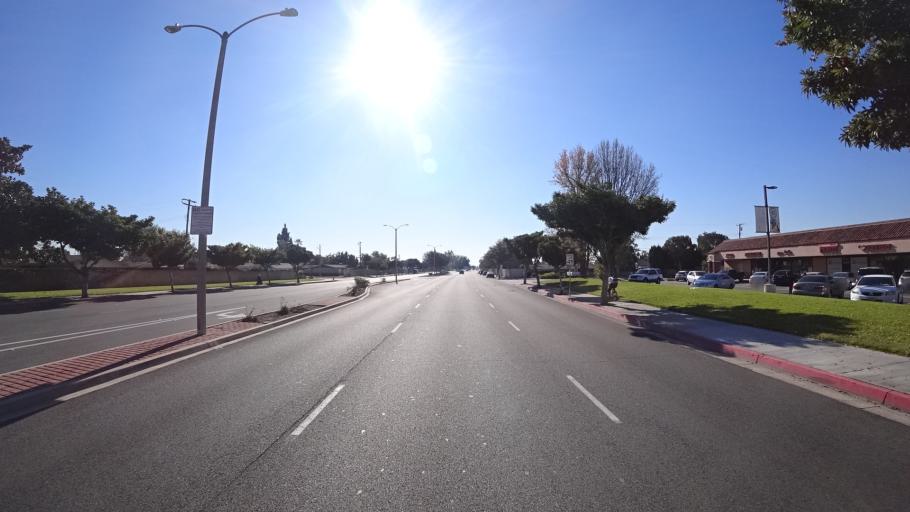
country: US
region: California
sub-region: Orange County
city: Garden Grove
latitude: 33.8020
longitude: -117.9592
